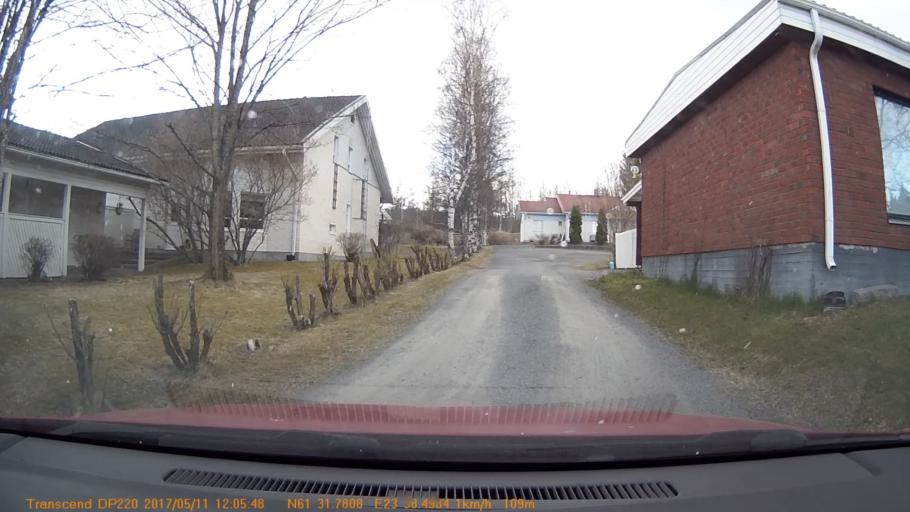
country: FI
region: Pirkanmaa
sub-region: Tampere
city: Yloejaervi
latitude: 61.5297
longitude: 23.6417
